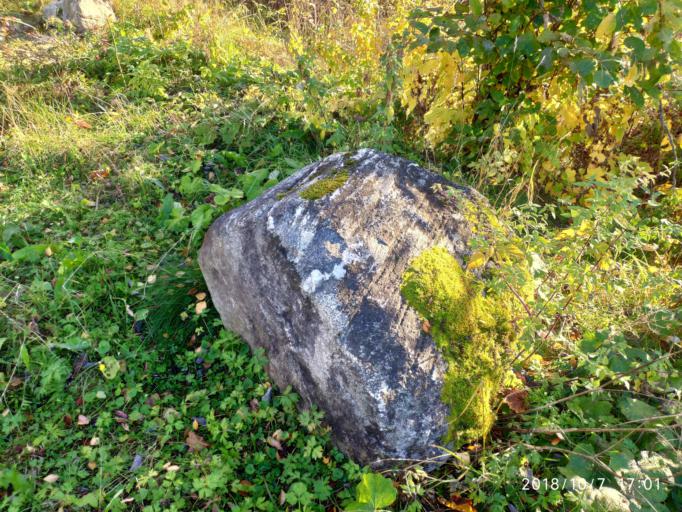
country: NO
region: Akershus
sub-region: Nes
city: Neskollen
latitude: 60.2161
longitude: 11.3565
